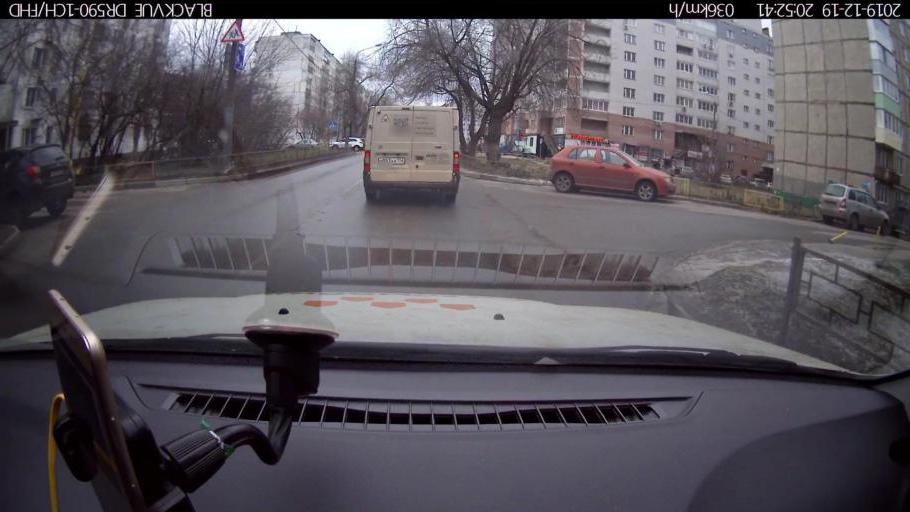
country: RU
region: Nizjnij Novgorod
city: Nizhniy Novgorod
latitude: 56.3319
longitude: 43.8734
